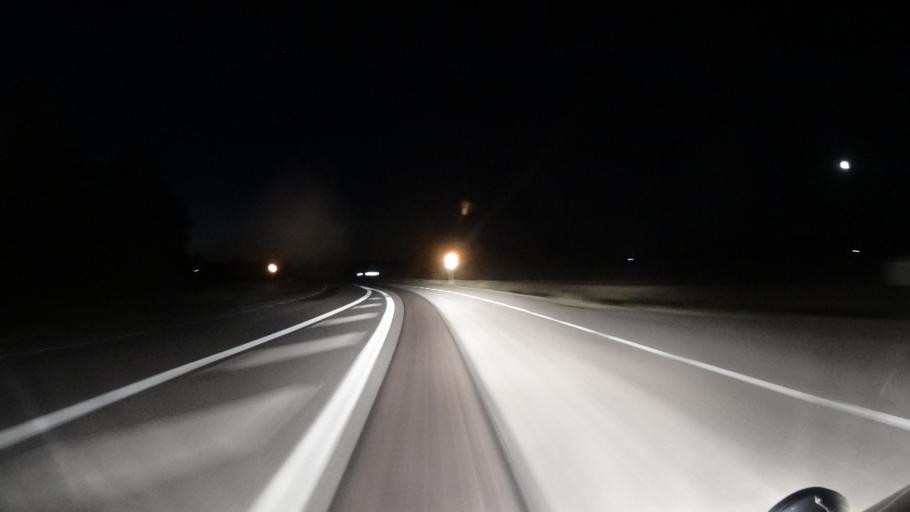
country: SE
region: OEstergoetland
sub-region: Odeshogs Kommun
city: OEdeshoeg
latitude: 58.2451
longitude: 14.7212
